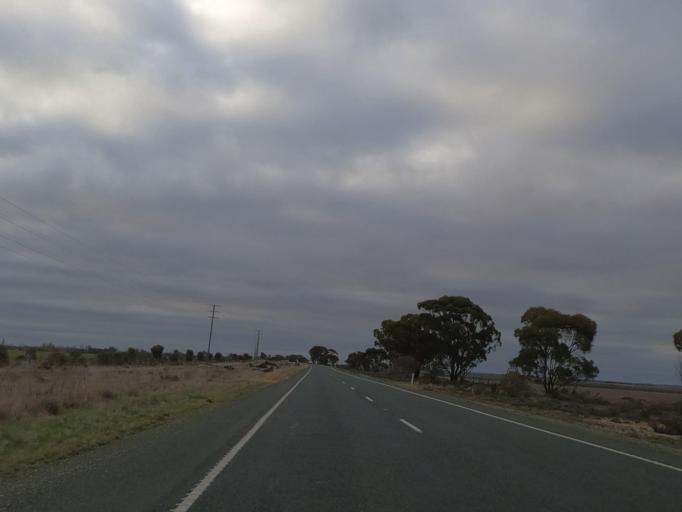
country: AU
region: Victoria
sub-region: Swan Hill
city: Swan Hill
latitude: -35.5778
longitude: 143.7884
